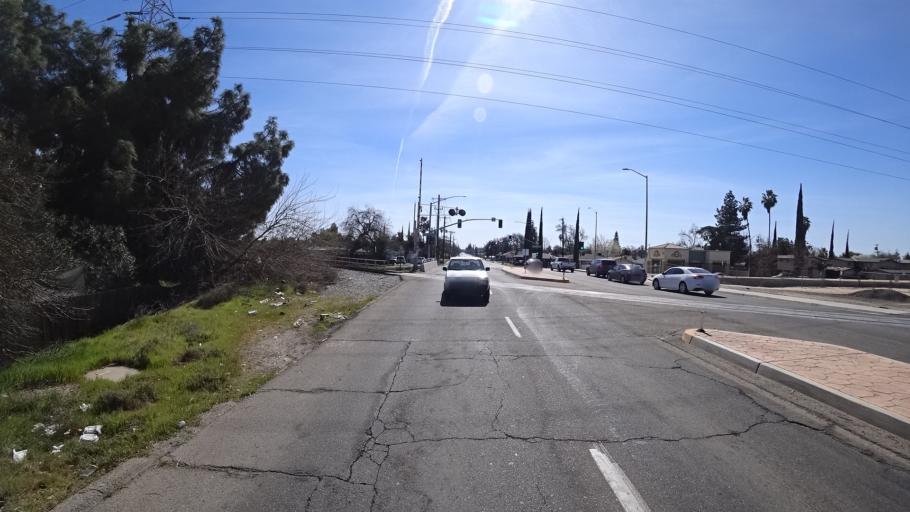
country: US
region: California
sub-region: Fresno County
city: Fresno
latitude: 36.7870
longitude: -119.8086
